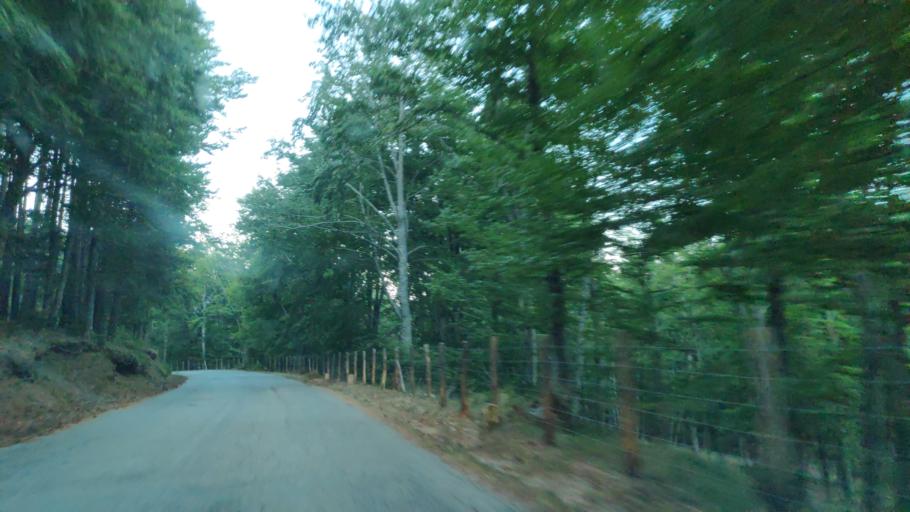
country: IT
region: Calabria
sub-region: Provincia di Vibo-Valentia
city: Nardodipace
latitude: 38.4892
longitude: 16.3738
